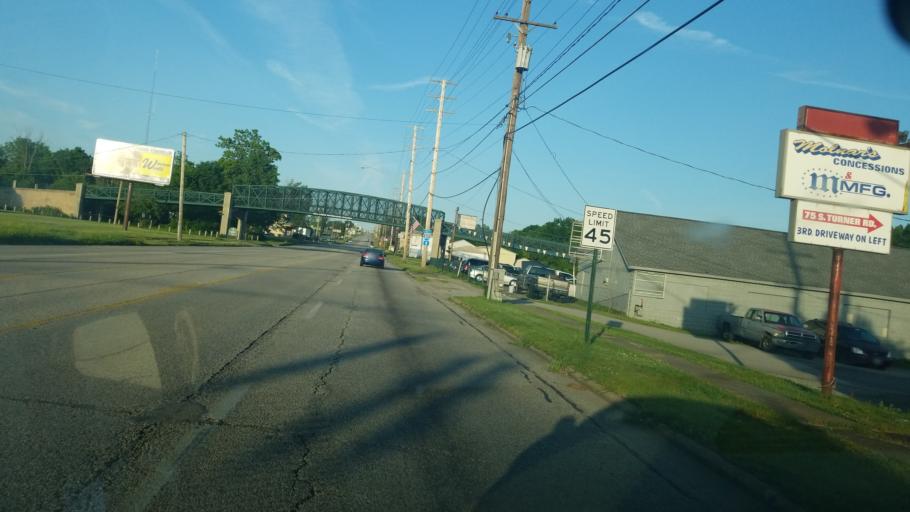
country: US
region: Ohio
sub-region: Mahoning County
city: Austintown
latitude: 41.0995
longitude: -80.7915
